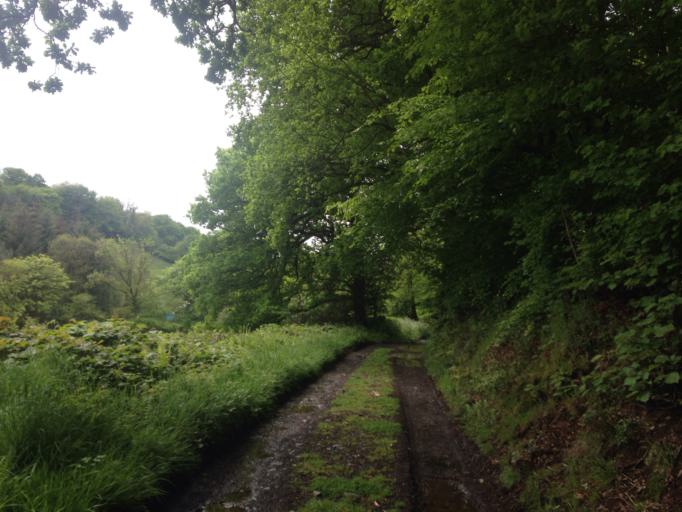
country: GB
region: Wales
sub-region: County of Ceredigion
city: Newcastle Emlyn
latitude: 52.0988
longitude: -4.4038
